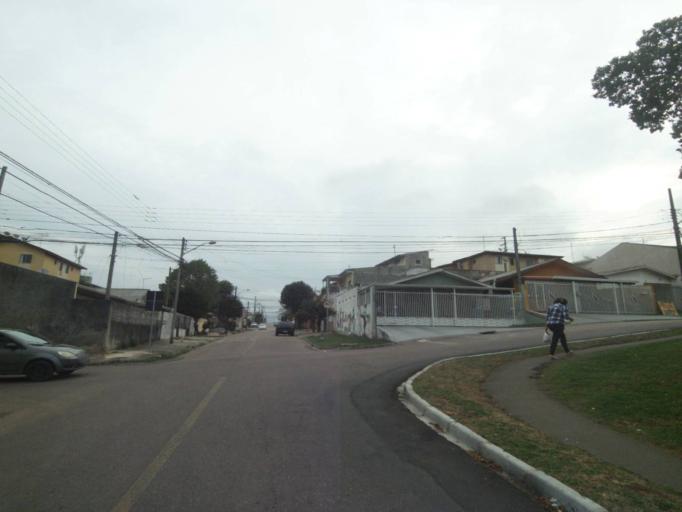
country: BR
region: Parana
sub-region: Sao Jose Dos Pinhais
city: Sao Jose dos Pinhais
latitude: -25.5480
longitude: -49.2640
